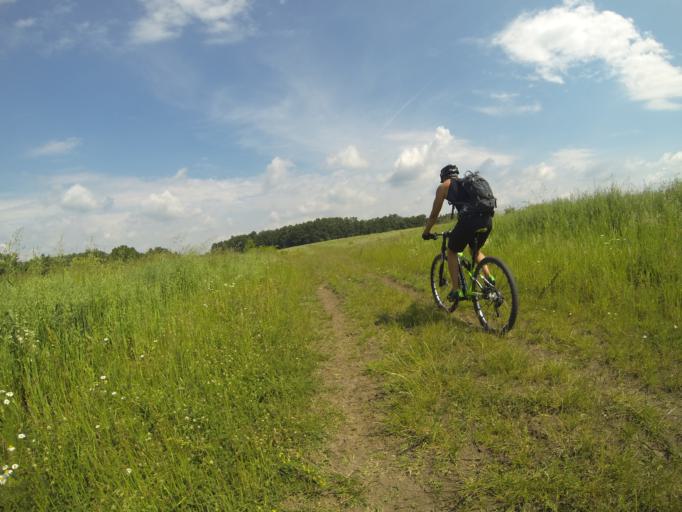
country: RO
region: Gorj
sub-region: Comuna Crusetu
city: Crusetu
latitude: 44.6305
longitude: 23.6098
